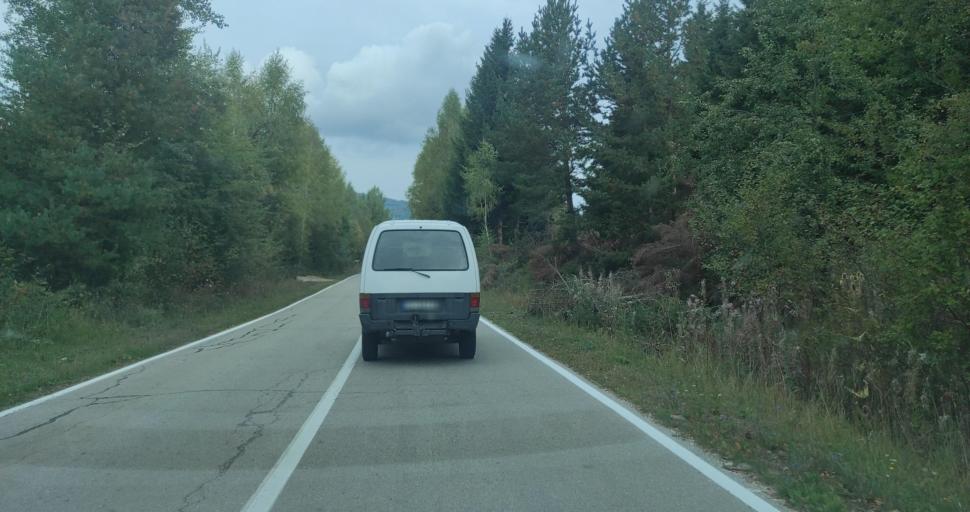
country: RS
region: Central Serbia
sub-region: Jablanicki Okrug
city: Crna Trava
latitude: 42.6825
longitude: 22.3141
